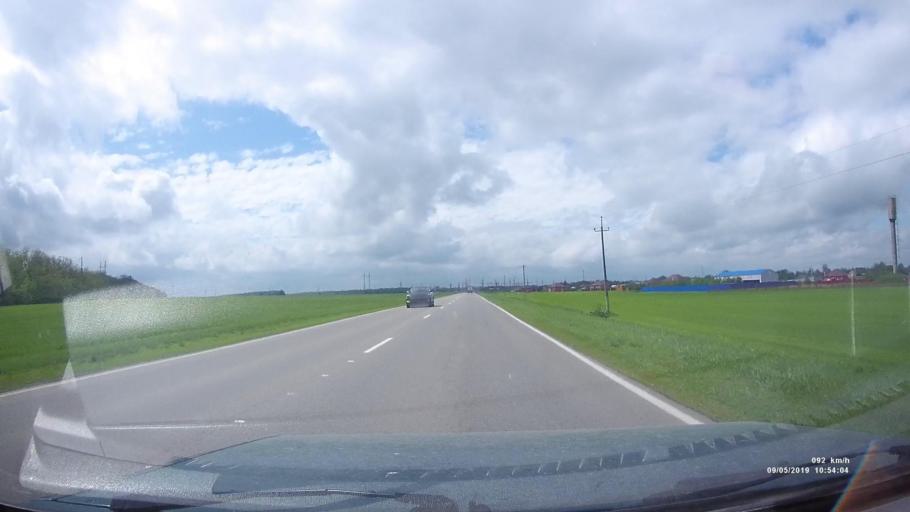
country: RU
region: Rostov
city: Peshkovo
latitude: 46.8819
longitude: 39.3350
